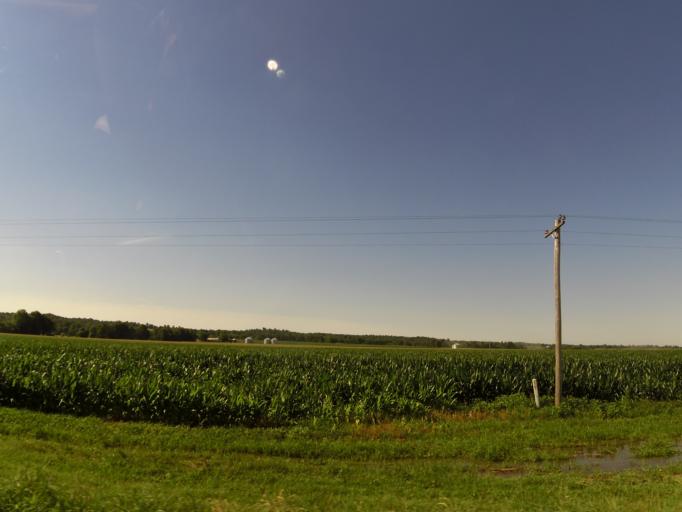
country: US
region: Arkansas
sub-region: Clay County
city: Piggott
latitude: 36.4337
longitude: -90.3525
